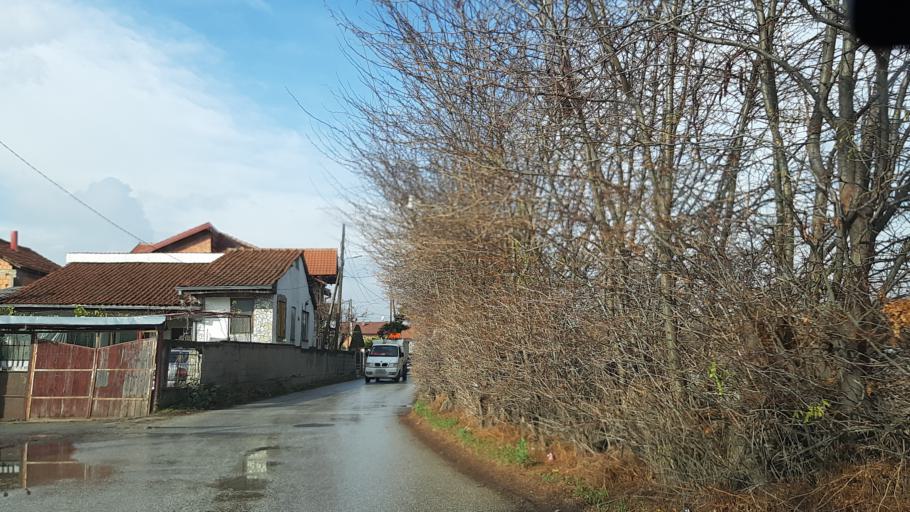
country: MK
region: Kisela Voda
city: Kisela Voda
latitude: 41.9817
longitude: 21.4906
